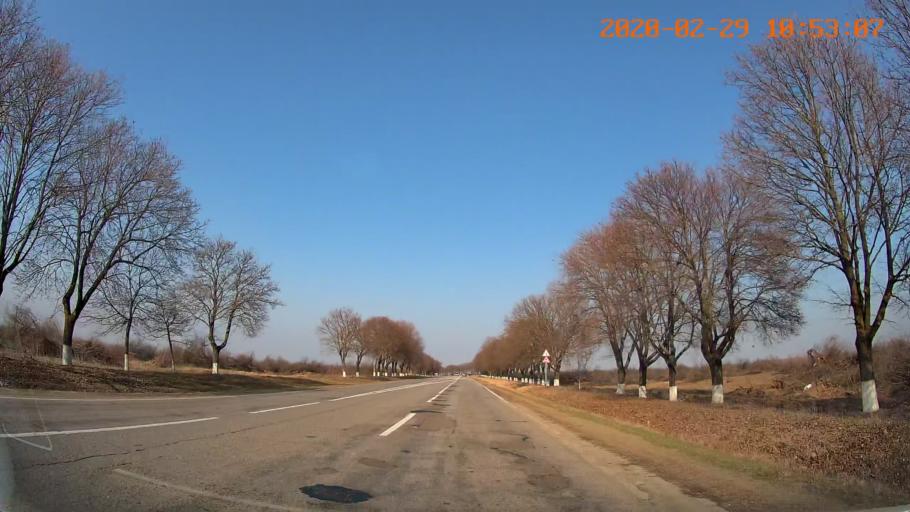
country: MD
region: Telenesti
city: Grigoriopol
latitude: 47.1125
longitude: 29.3407
